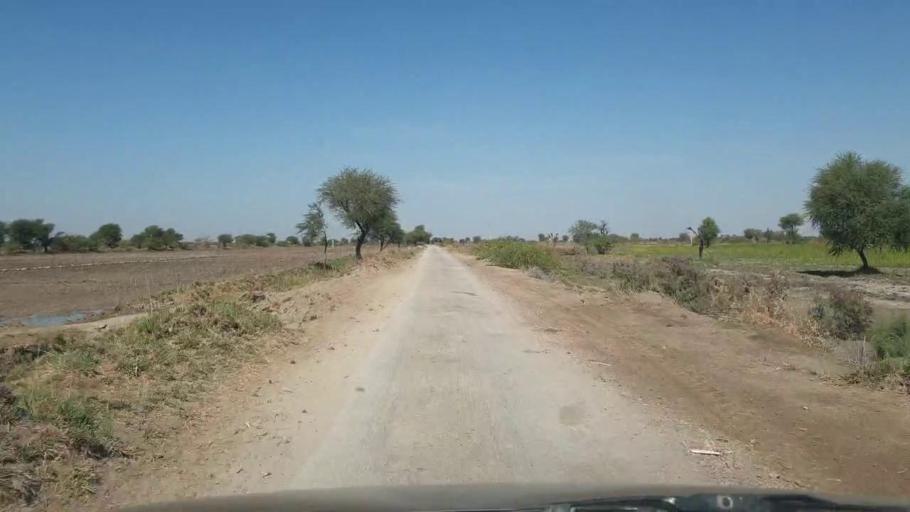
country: PK
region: Sindh
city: Dhoro Naro
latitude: 25.4329
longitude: 69.6192
